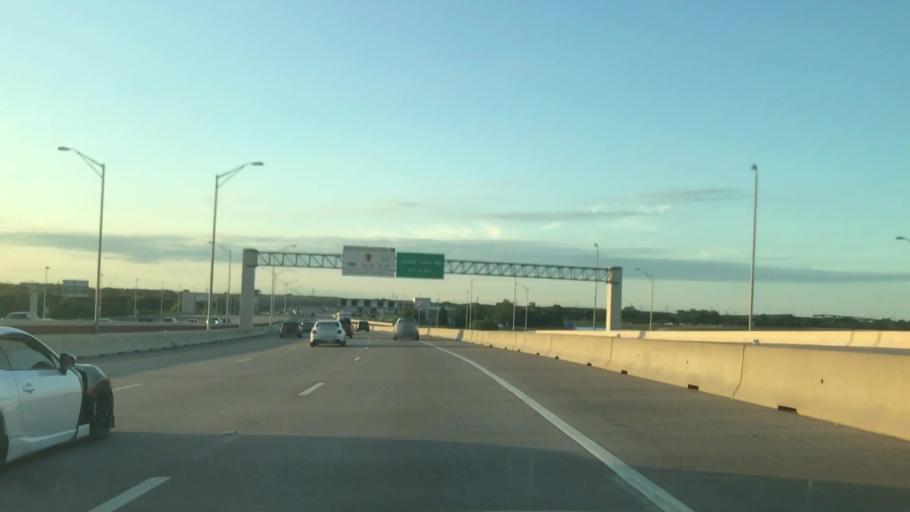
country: US
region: Texas
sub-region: Dallas County
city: Carrollton
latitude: 32.9561
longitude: -96.9267
